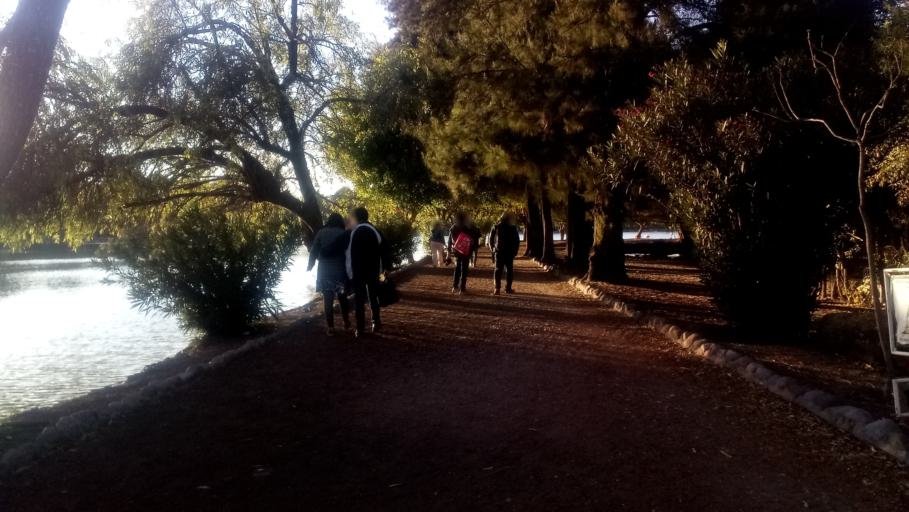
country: MX
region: Puebla
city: Puebla
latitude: 19.0065
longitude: -98.2121
